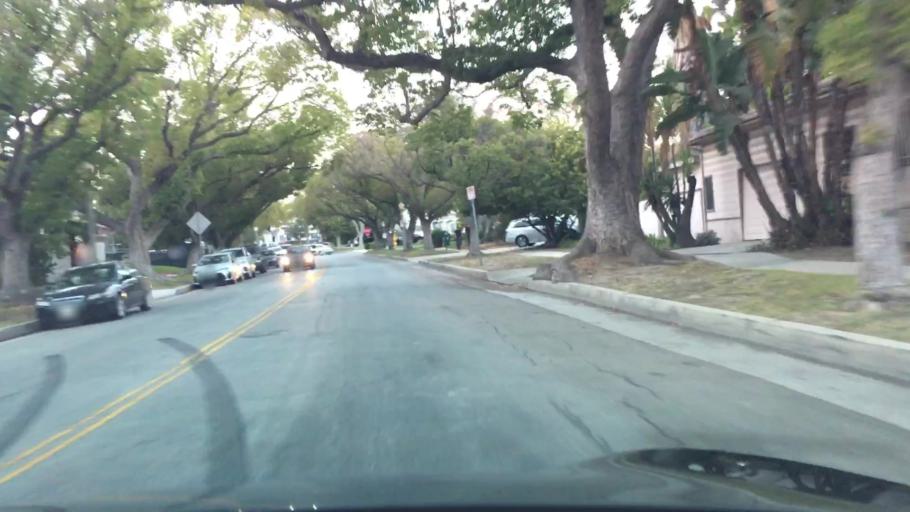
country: US
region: California
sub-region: Los Angeles County
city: Culver City
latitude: 34.0466
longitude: -118.3902
